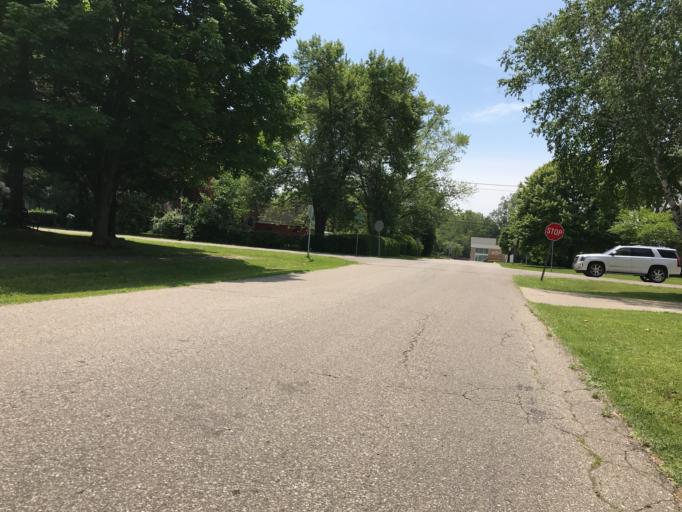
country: US
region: Michigan
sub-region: Oakland County
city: Southfield
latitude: 42.4743
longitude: -83.2341
